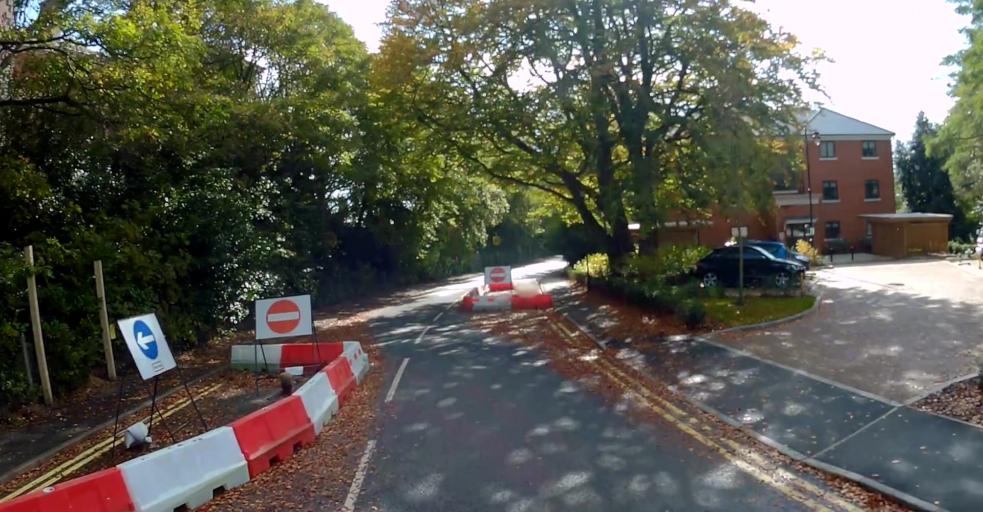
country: GB
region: England
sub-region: Hampshire
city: Aldershot
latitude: 51.2535
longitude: -0.7610
